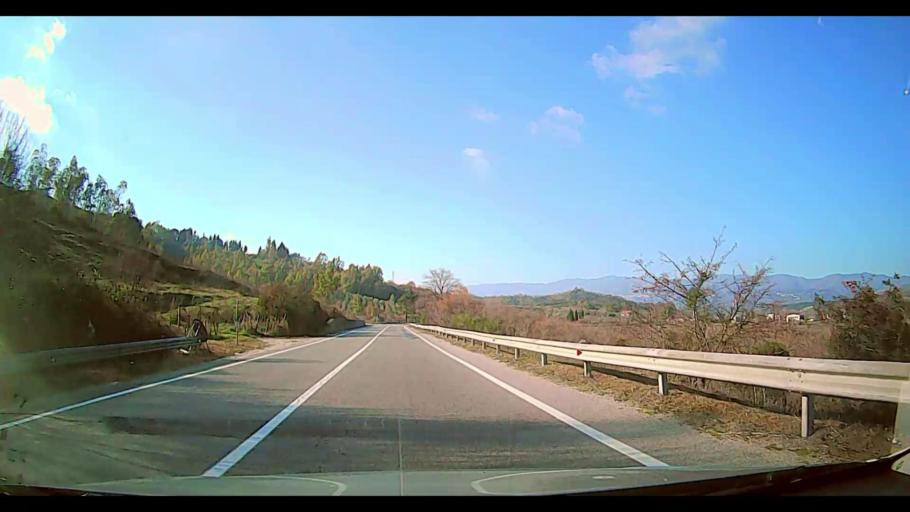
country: IT
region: Calabria
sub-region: Provincia di Crotone
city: Belvedere Spinello
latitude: 39.1906
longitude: 16.8787
